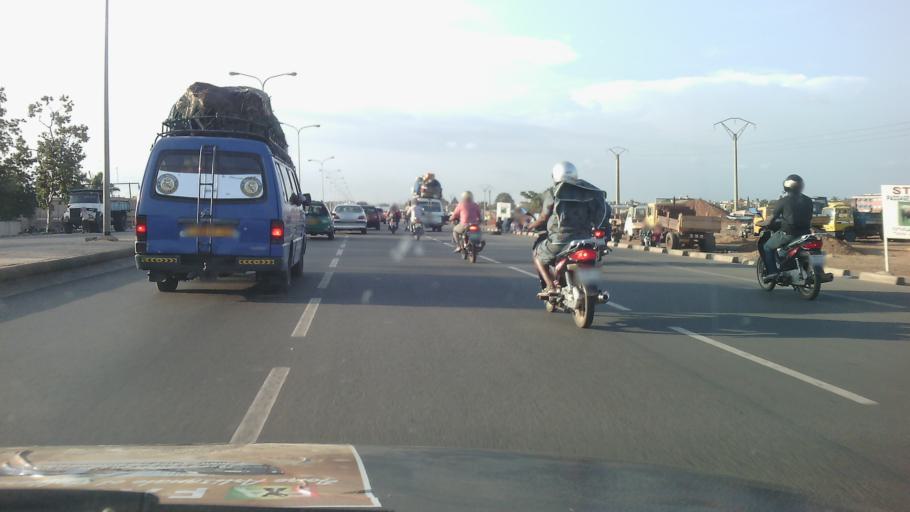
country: TG
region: Maritime
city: Lome
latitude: 6.2450
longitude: 1.2098
